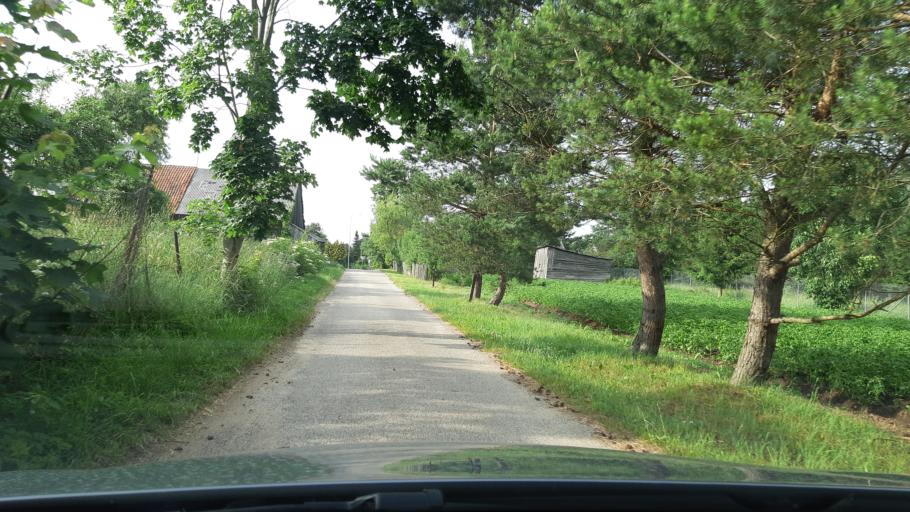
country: LT
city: Kybartai
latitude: 54.4533
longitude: 22.7204
